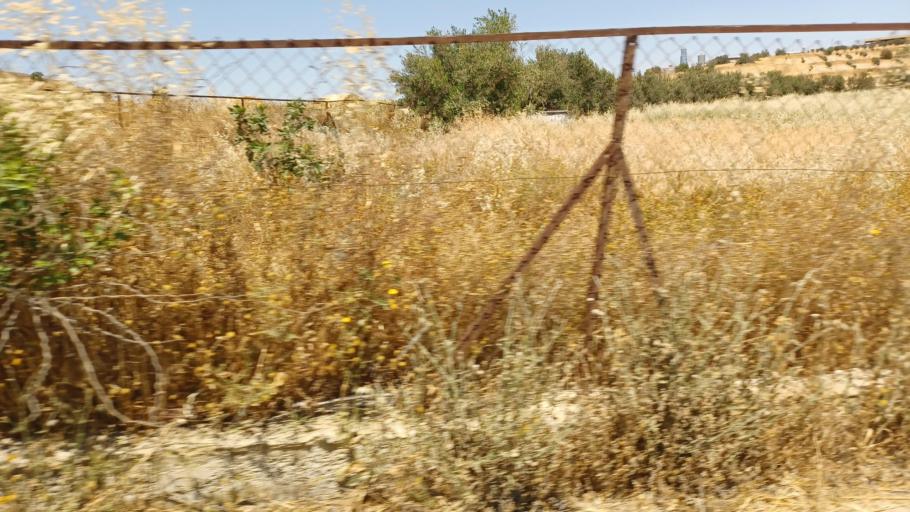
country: CY
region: Larnaka
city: Athienou
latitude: 35.0399
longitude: 33.5380
